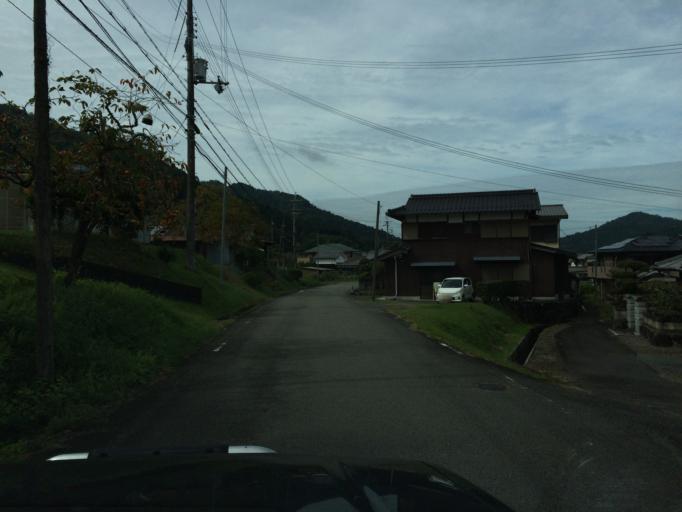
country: JP
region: Hyogo
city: Sasayama
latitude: 35.0723
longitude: 135.3660
